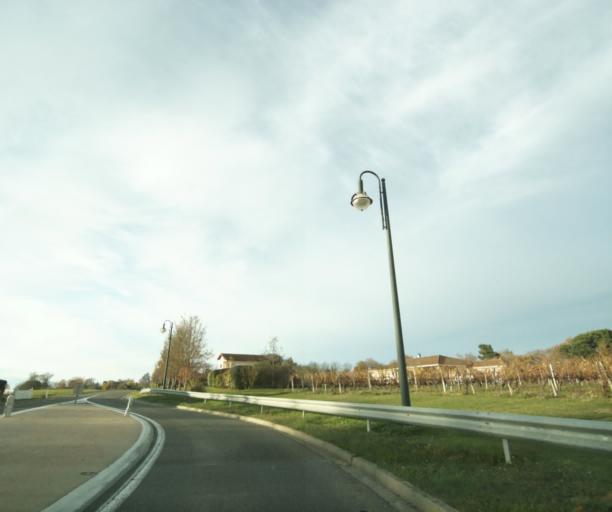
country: FR
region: Midi-Pyrenees
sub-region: Departement du Gers
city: Cazaubon
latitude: 43.9318
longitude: -0.0526
